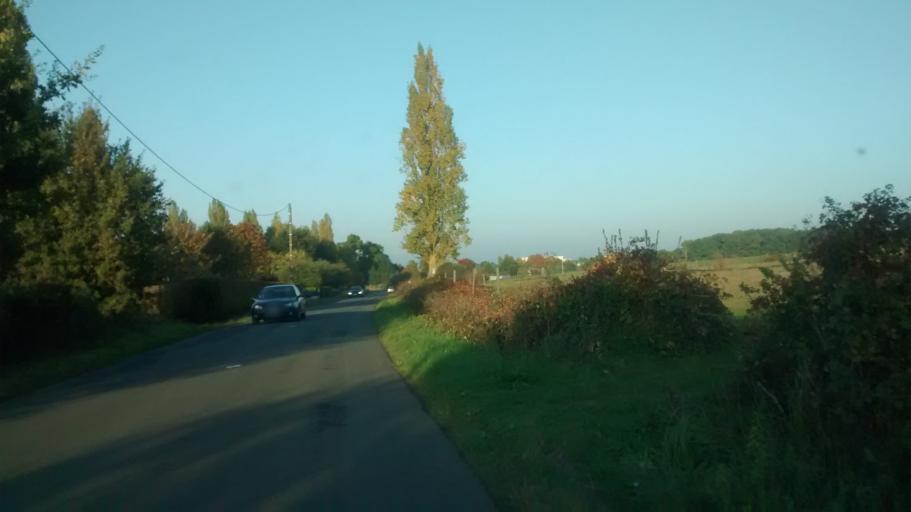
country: FR
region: Brittany
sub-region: Departement d'Ille-et-Vilaine
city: La Chapelle-Thouarault
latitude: 48.1154
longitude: -1.8415
